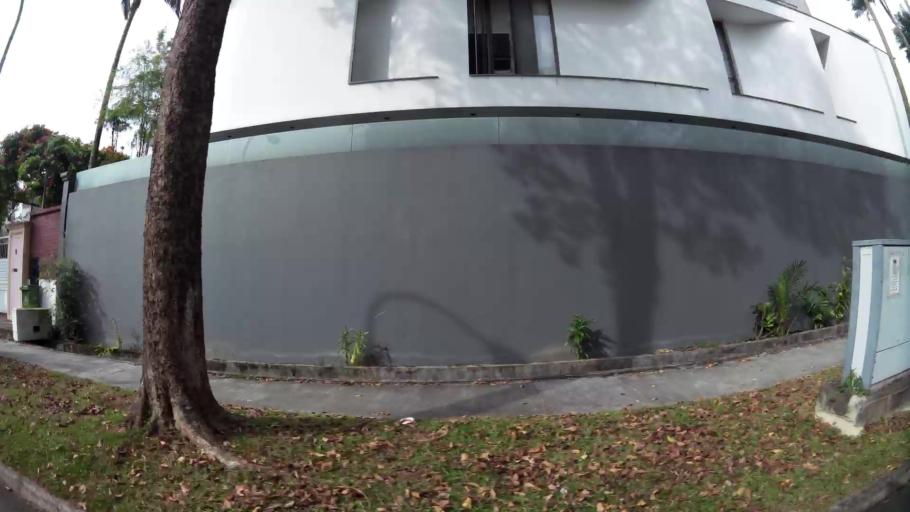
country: SG
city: Singapore
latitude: 1.3229
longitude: 103.8225
